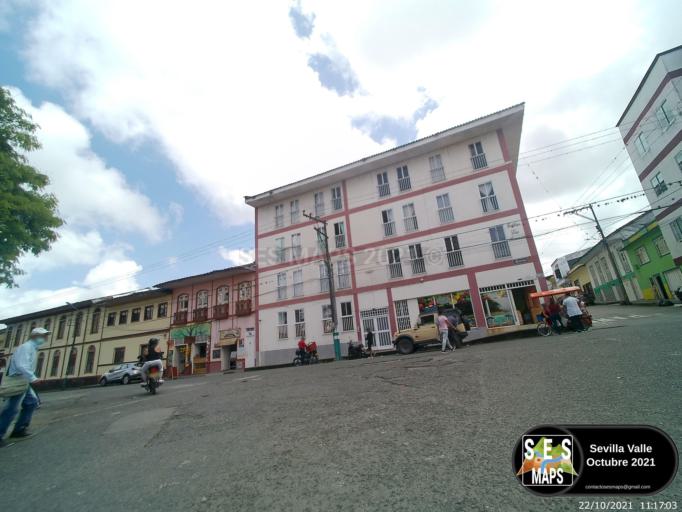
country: CO
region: Valle del Cauca
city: Sevilla
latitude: 4.2630
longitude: -75.9316
